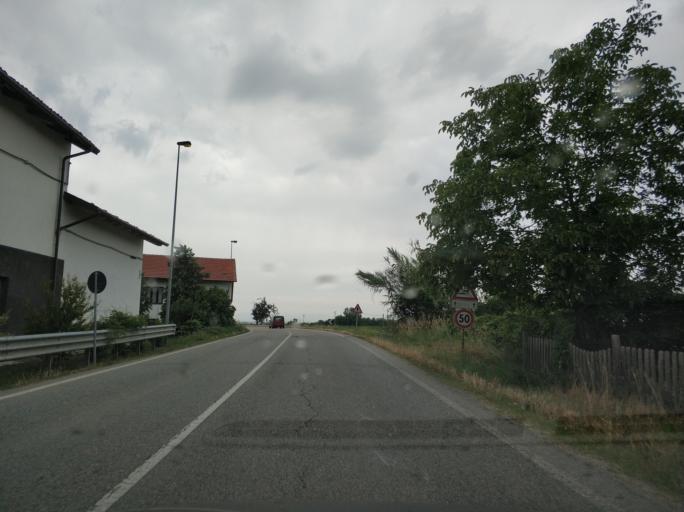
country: IT
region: Piedmont
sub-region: Provincia di Torino
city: Pralormo
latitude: 44.8698
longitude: 7.8957
